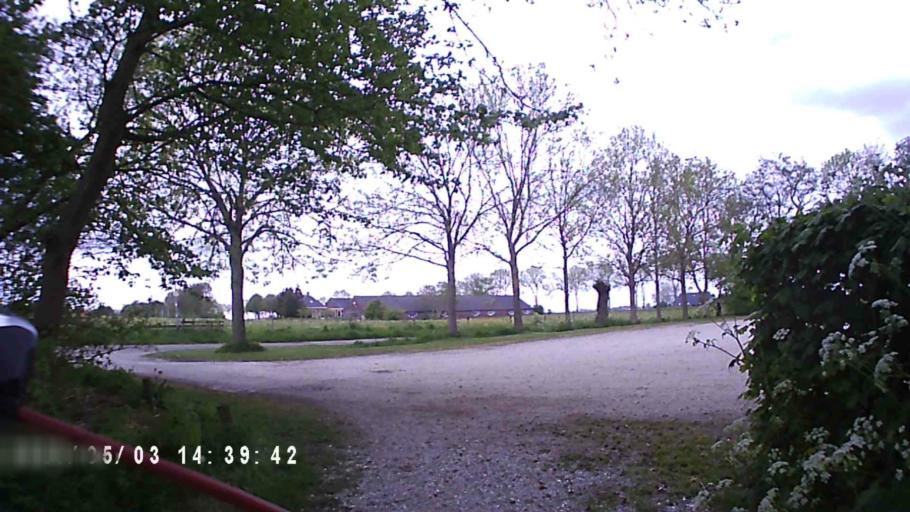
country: NL
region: Groningen
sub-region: Gemeente De Marne
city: Ulrum
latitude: 53.3621
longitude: 6.3893
